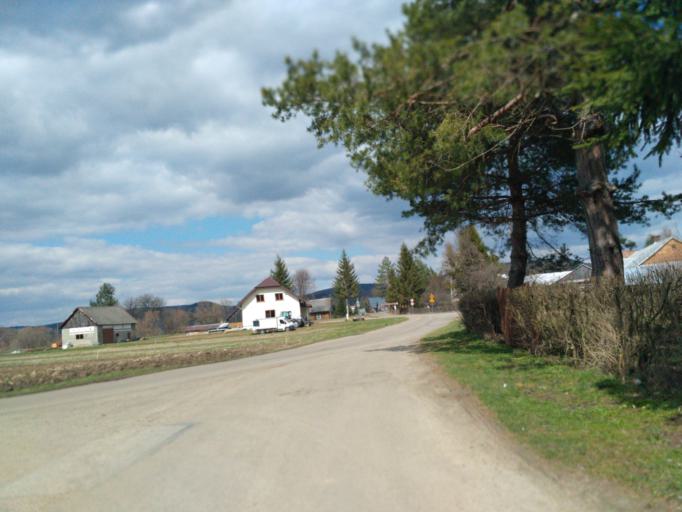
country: PL
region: Subcarpathian Voivodeship
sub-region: Powiat sanocki
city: Tyrawa Woloska
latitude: 49.6450
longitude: 22.2984
